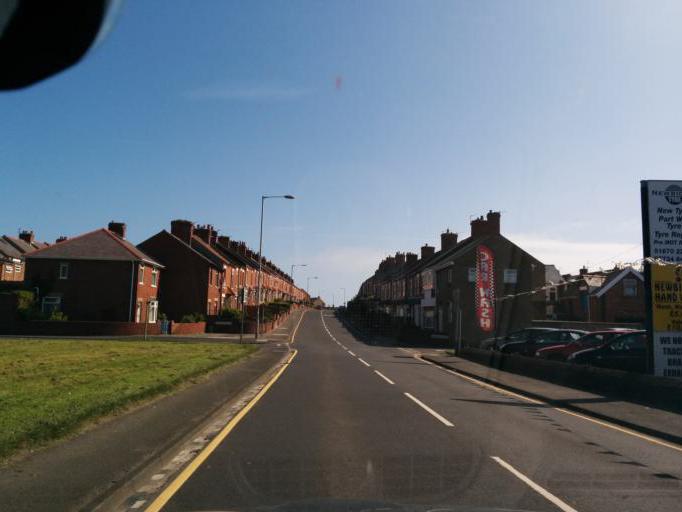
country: GB
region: England
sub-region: Northumberland
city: Newbiggin-by-the-Sea
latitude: 55.1789
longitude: -1.5202
